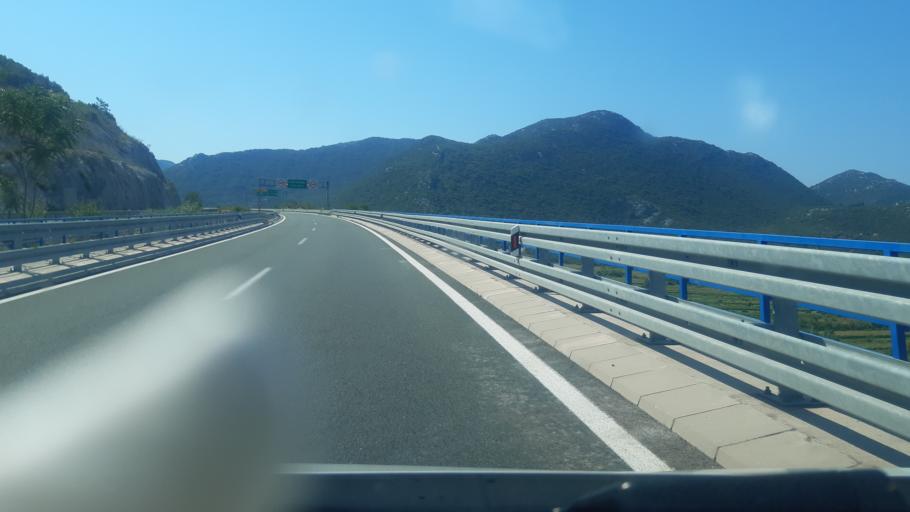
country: HR
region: Dubrovacko-Neretvanska
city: Komin
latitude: 43.1080
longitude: 17.4786
